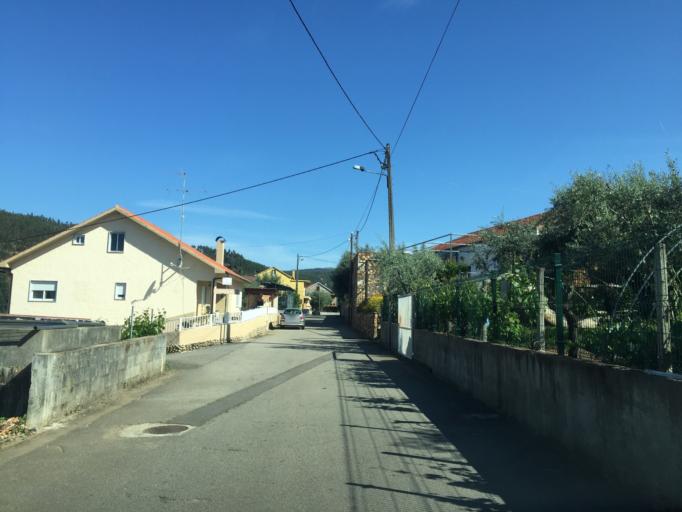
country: PT
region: Coimbra
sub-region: Pampilhosa da Serra
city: Pampilhosa da Serra
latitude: 40.0672
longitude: -7.8018
